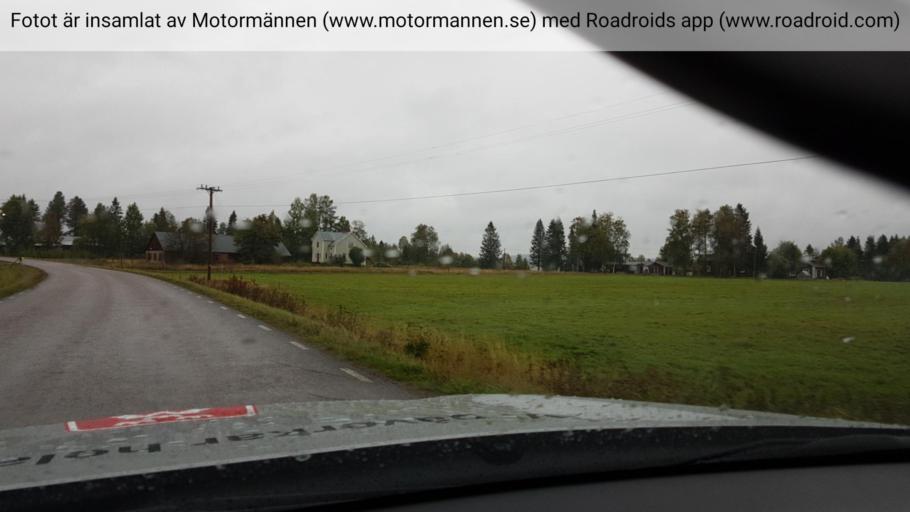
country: SE
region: Norrbotten
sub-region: Lulea Kommun
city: Gammelstad
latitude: 65.7602
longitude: 22.0968
